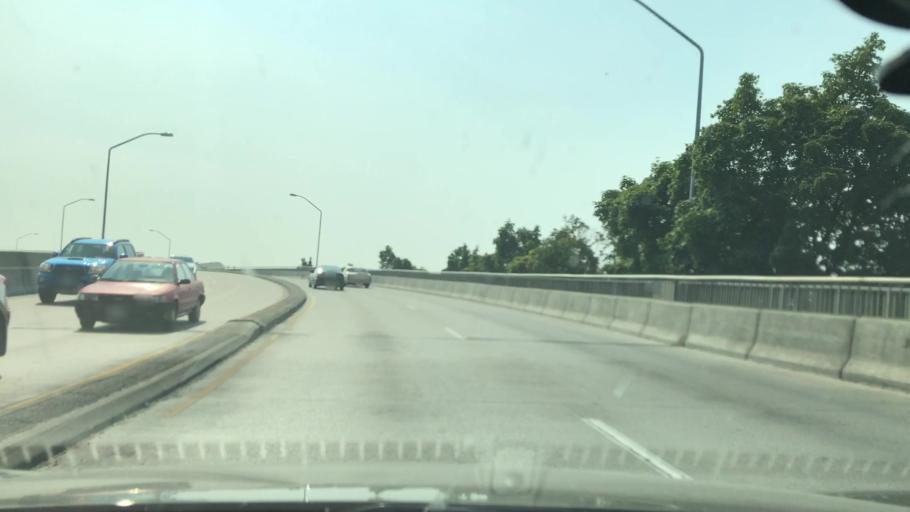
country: US
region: Washington
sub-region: Spokane County
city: Spokane
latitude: 47.6707
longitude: -117.3635
